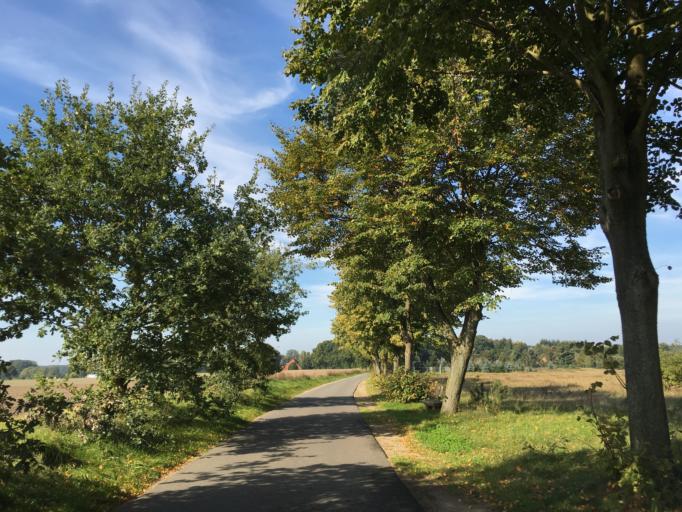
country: DE
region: Lower Saxony
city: Scharnebeck
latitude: 53.2709
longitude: 10.4824
